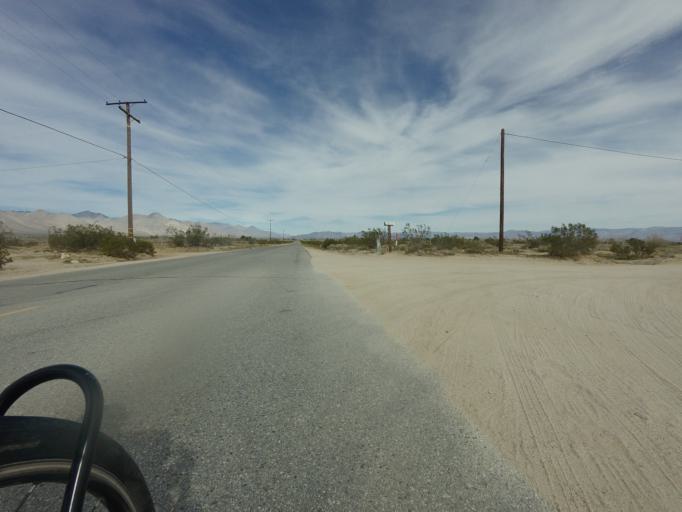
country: US
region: California
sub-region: Kern County
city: Inyokern
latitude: 35.6957
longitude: -117.8268
